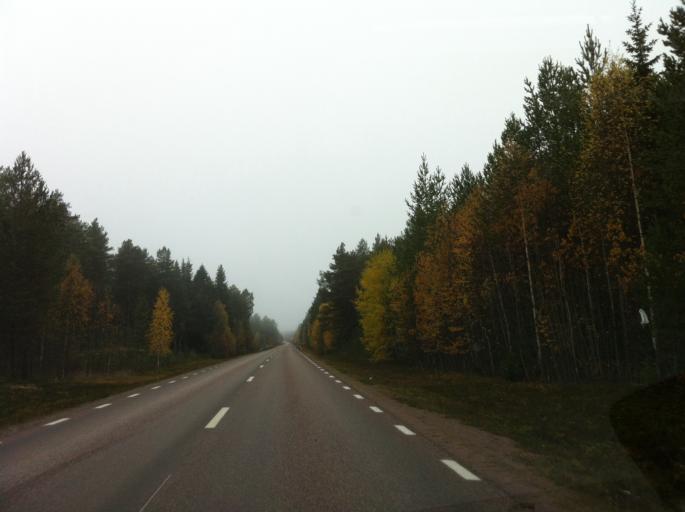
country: NO
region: Hedmark
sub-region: Trysil
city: Innbygda
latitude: 61.6950
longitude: 13.1092
